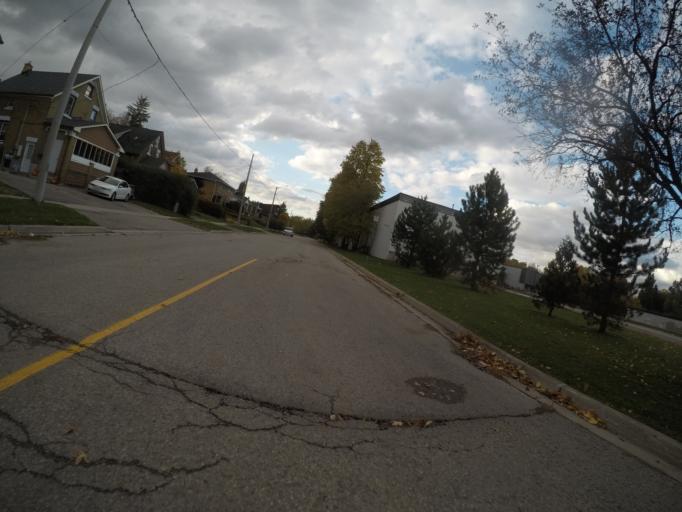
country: CA
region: Ontario
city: Kitchener
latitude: 43.4403
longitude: -80.4797
